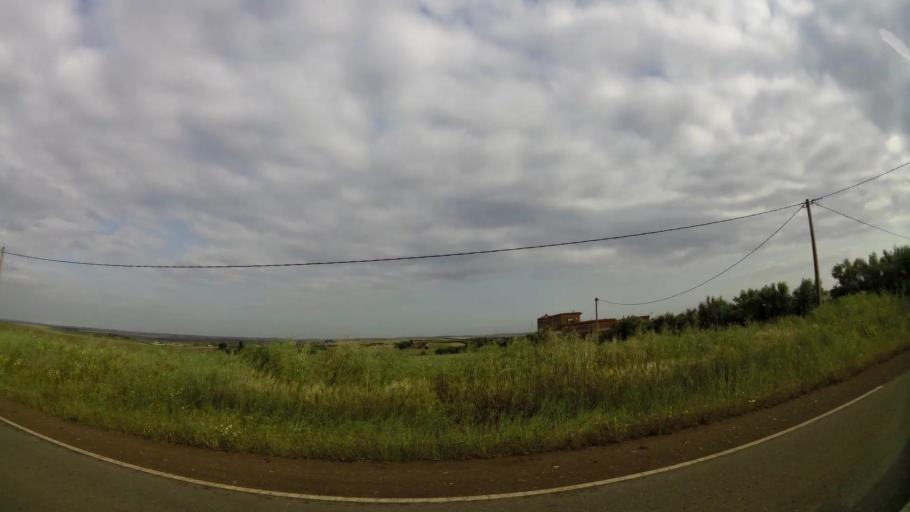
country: MA
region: Rabat-Sale-Zemmour-Zaer
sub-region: Khemisset
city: Khemisset
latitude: 33.7608
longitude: -6.1779
